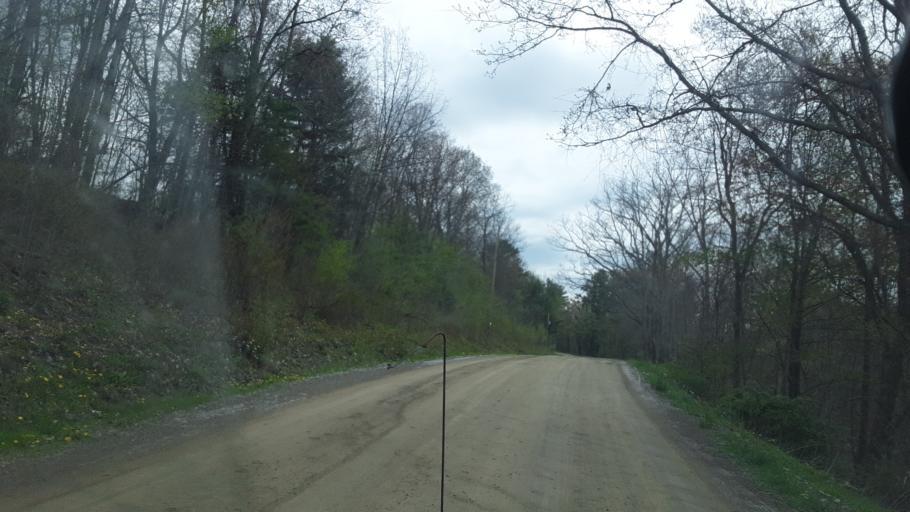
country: US
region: New York
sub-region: Steuben County
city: Addison
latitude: 42.0966
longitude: -77.3300
